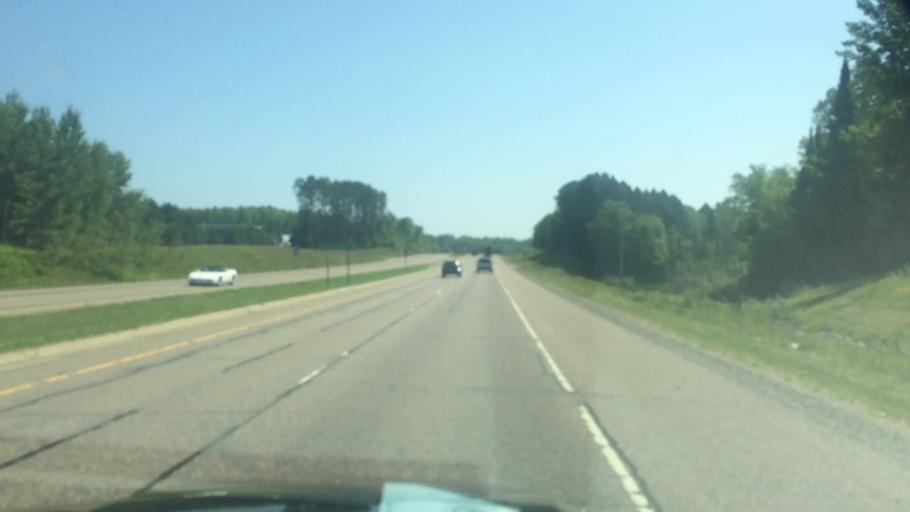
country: US
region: Wisconsin
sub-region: Oneida County
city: Rhinelander
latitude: 45.6192
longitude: -89.4825
